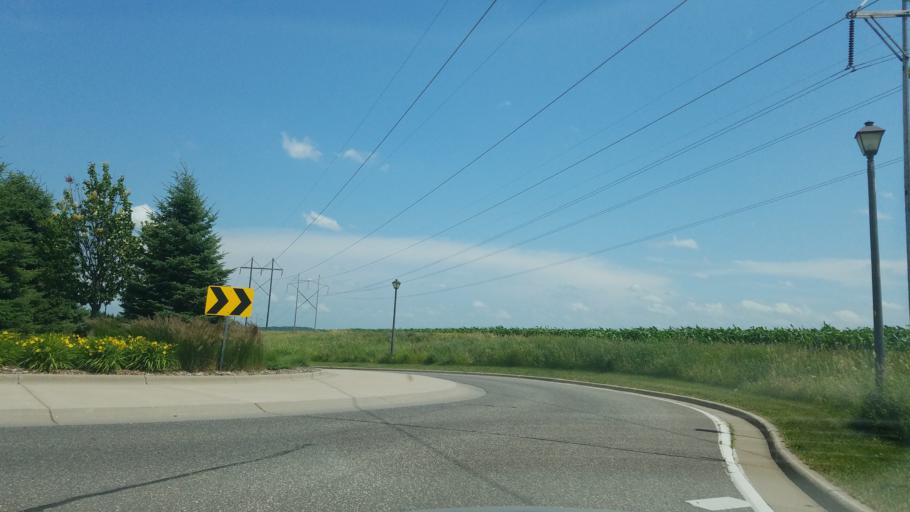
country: US
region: Minnesota
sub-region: Washington County
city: Woodbury
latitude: 44.8838
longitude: -92.9309
